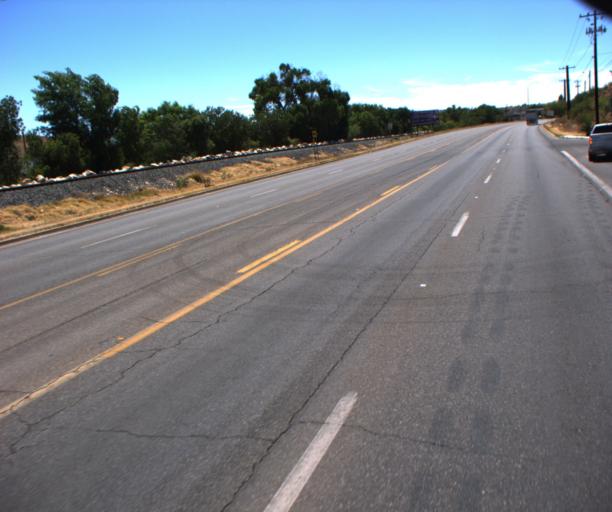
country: US
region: Arizona
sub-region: Santa Cruz County
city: Nogales
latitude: 31.3734
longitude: -110.9345
